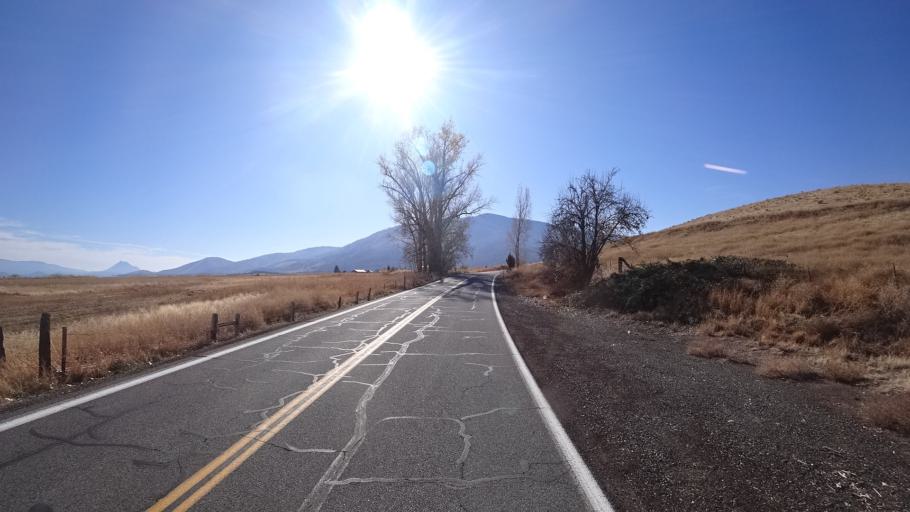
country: US
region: California
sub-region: Siskiyou County
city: Weed
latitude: 41.5126
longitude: -122.5255
